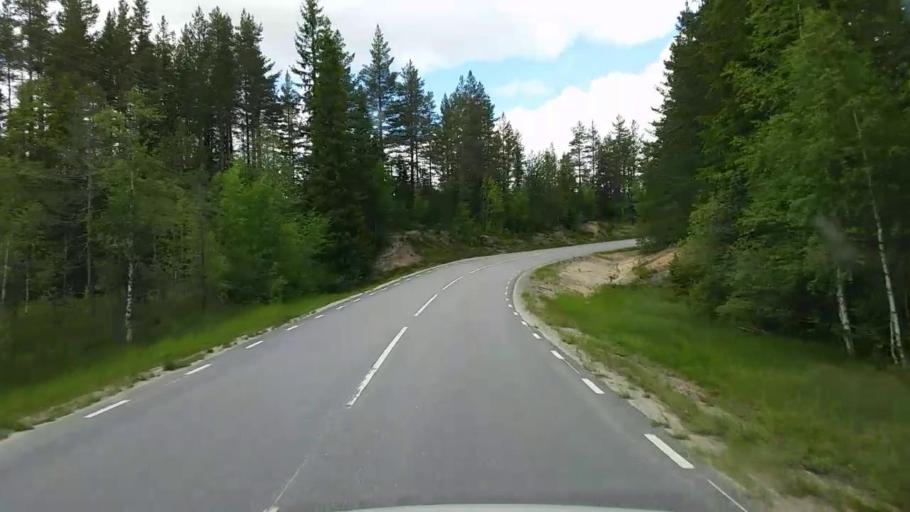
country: SE
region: Gaevleborg
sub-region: Bollnas Kommun
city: Vittsjo
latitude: 61.1143
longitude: 16.1477
